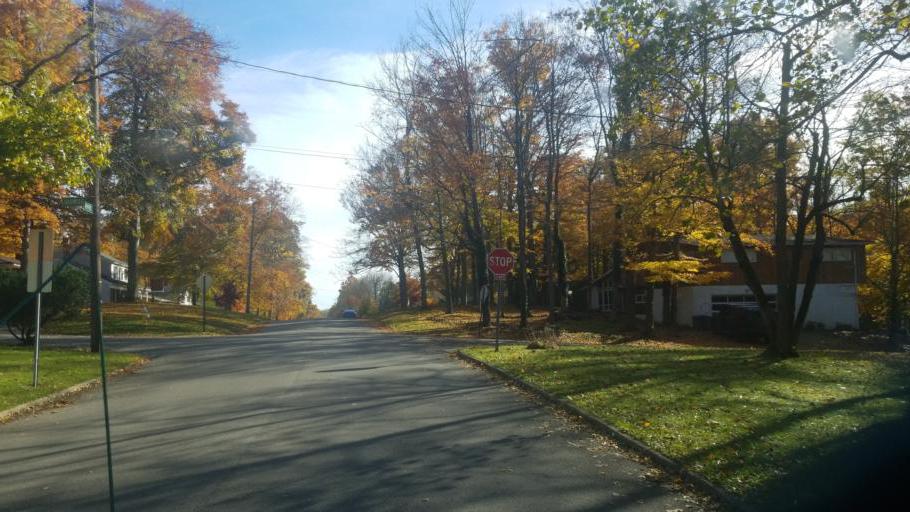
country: US
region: Ohio
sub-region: Richland County
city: Mansfield
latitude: 40.7261
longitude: -82.5231
